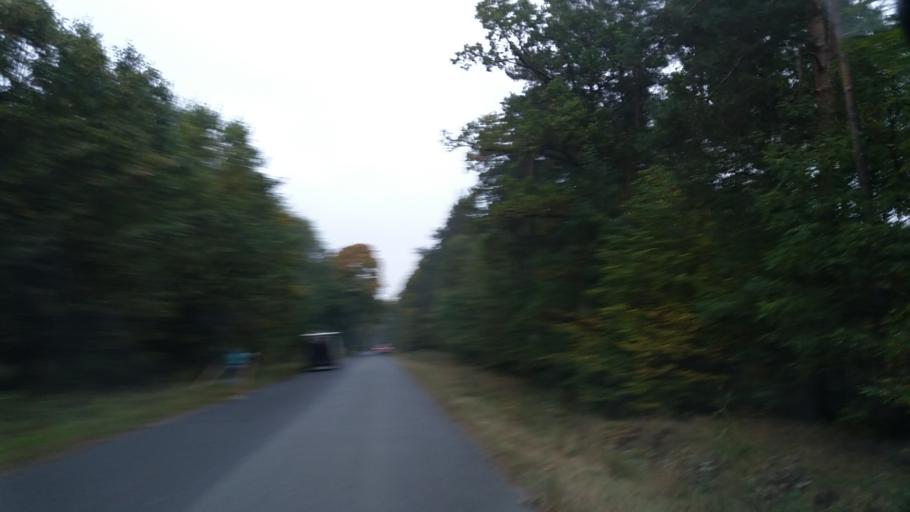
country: PL
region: Lubusz
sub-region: Powiat strzelecko-drezdenecki
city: Dobiegniew
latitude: 53.0610
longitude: 15.7619
